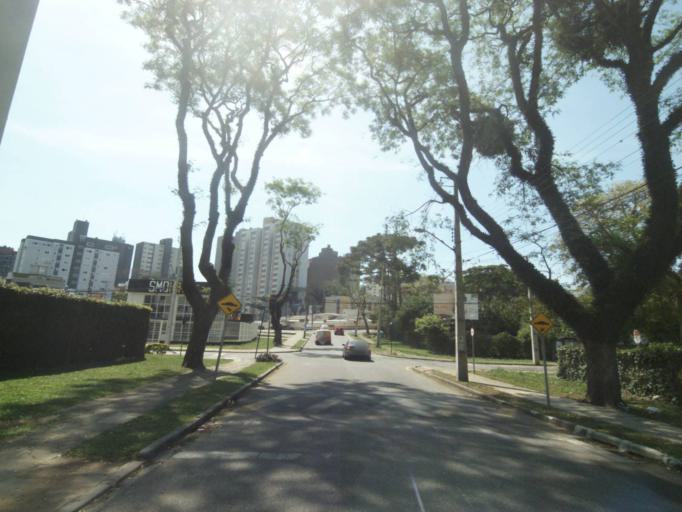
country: BR
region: Parana
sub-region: Curitiba
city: Curitiba
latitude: -25.4711
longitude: -49.2898
